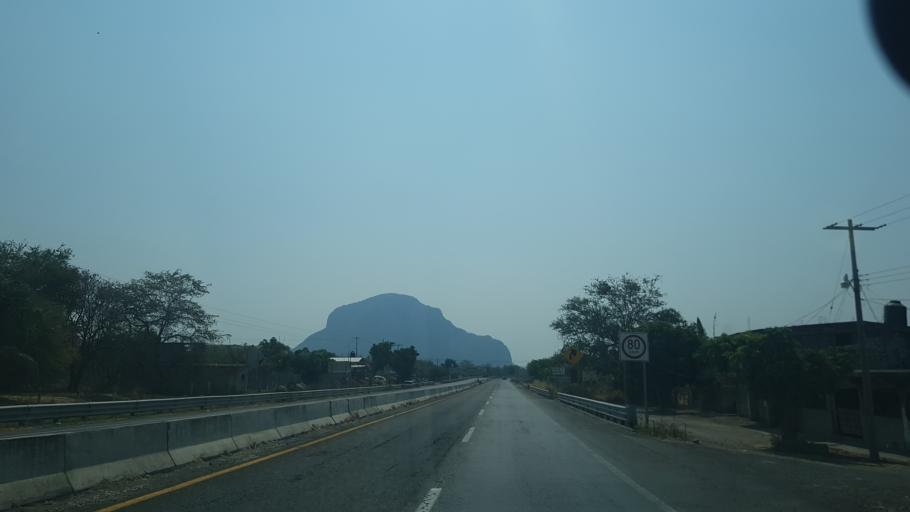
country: MX
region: Morelos
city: Amayuca
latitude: 18.7151
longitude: -98.7889
